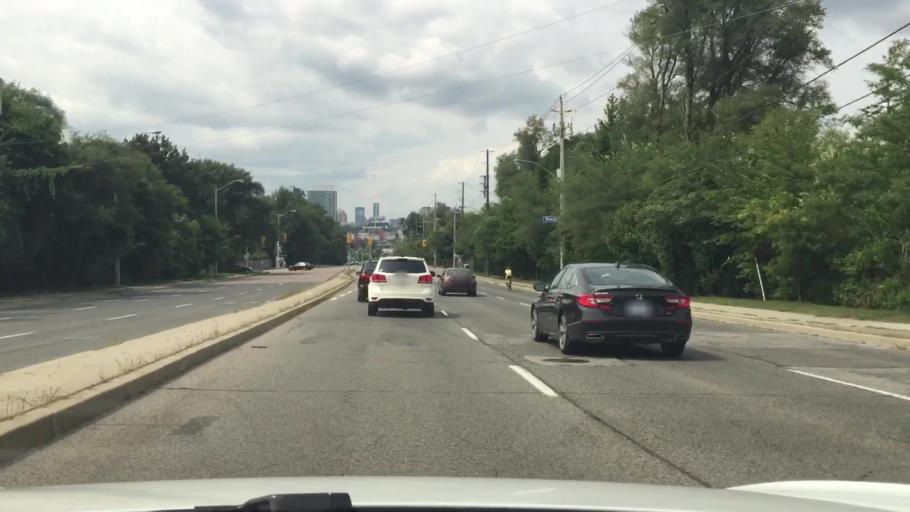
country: CA
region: Ontario
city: Willowdale
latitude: 43.7742
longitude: -79.3515
